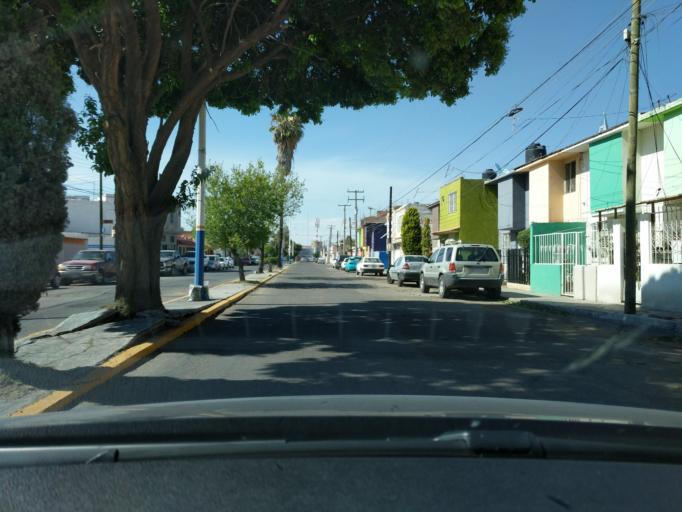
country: MX
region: Durango
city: Victoria de Durango
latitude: 24.0059
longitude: -104.6544
